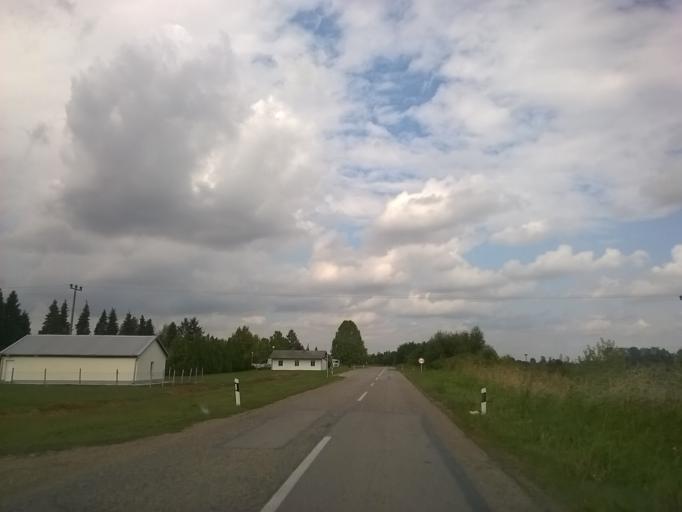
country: RS
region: Autonomna Pokrajina Vojvodina
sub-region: Juznobanatski Okrug
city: Plandiste
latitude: 45.2130
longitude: 21.1085
